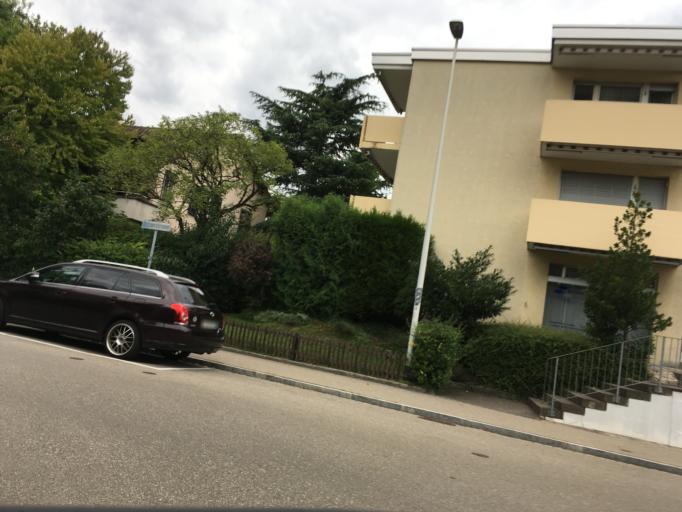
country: CH
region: Zurich
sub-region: Bezirk Uster
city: Dubendorf
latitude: 47.3947
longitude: 8.6222
